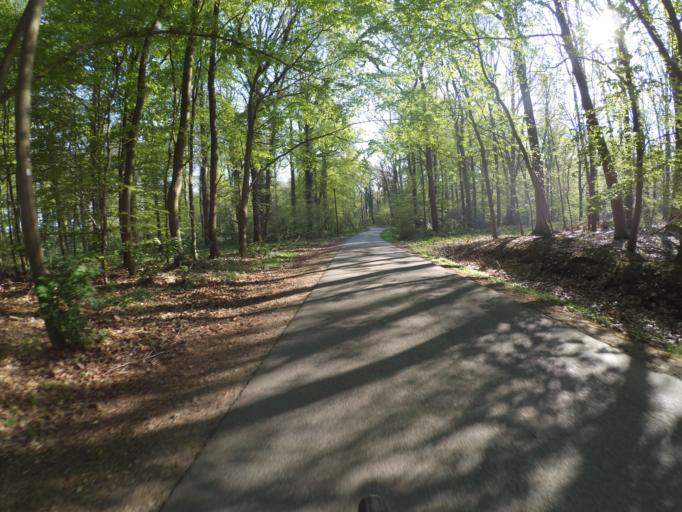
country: DE
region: North Rhine-Westphalia
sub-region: Regierungsbezirk Munster
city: Senden
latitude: 51.8538
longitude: 7.5128
